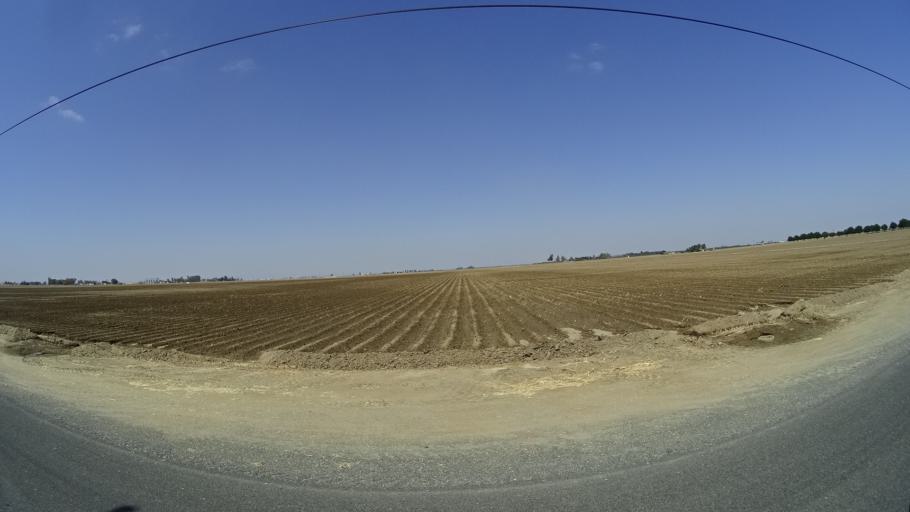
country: US
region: California
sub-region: Kings County
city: Home Garden
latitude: 36.2359
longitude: -119.6190
